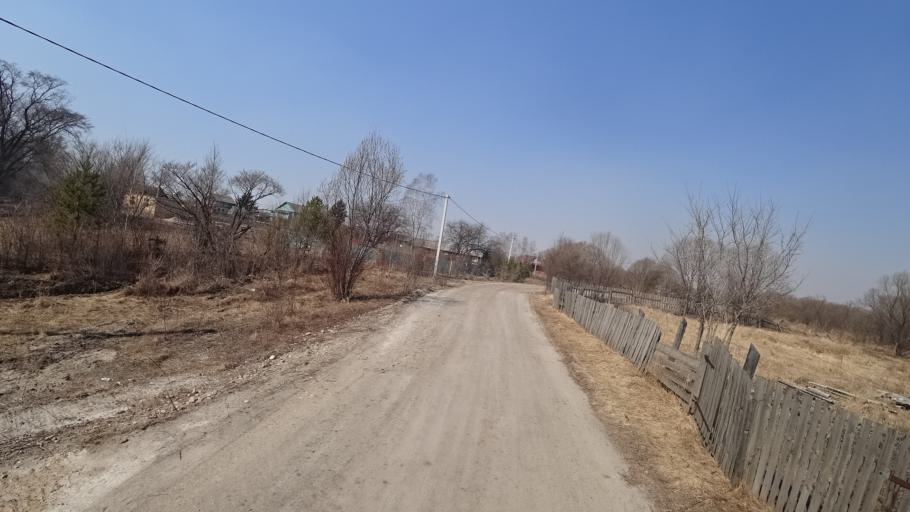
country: RU
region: Amur
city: Novobureyskiy
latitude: 49.7761
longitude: 129.8490
